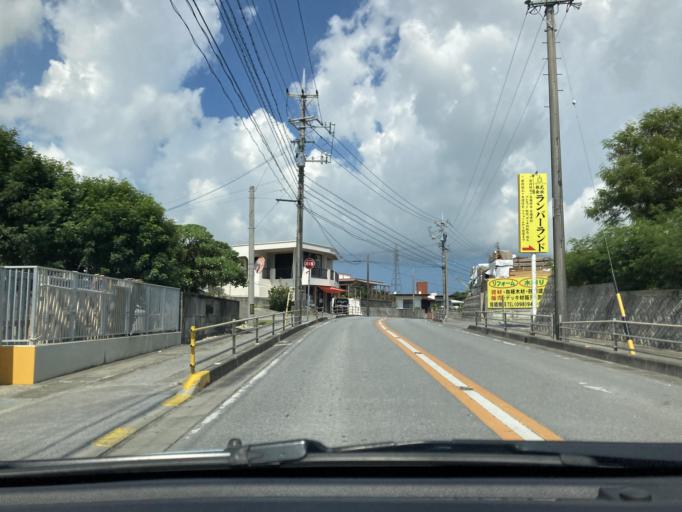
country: JP
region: Okinawa
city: Tomigusuku
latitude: 26.1608
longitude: 127.7408
